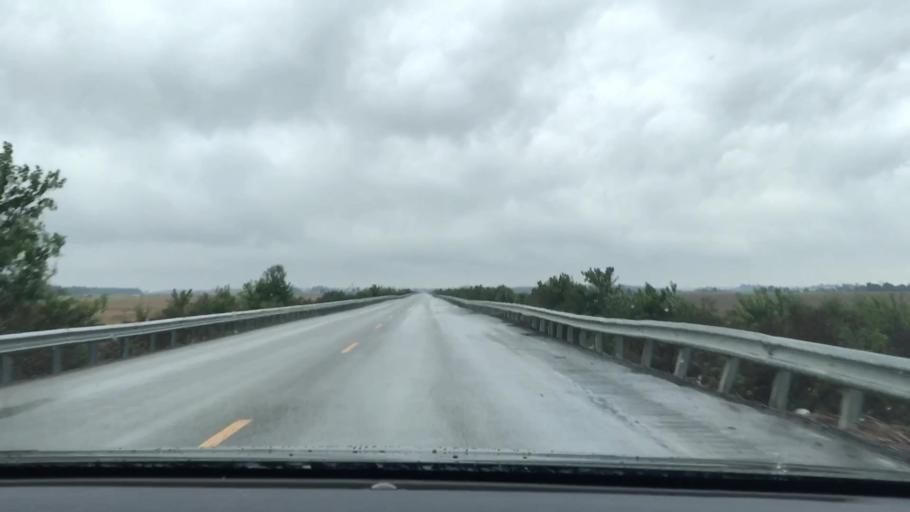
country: US
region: Kentucky
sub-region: McLean County
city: Calhoun
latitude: 37.3901
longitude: -87.3189
